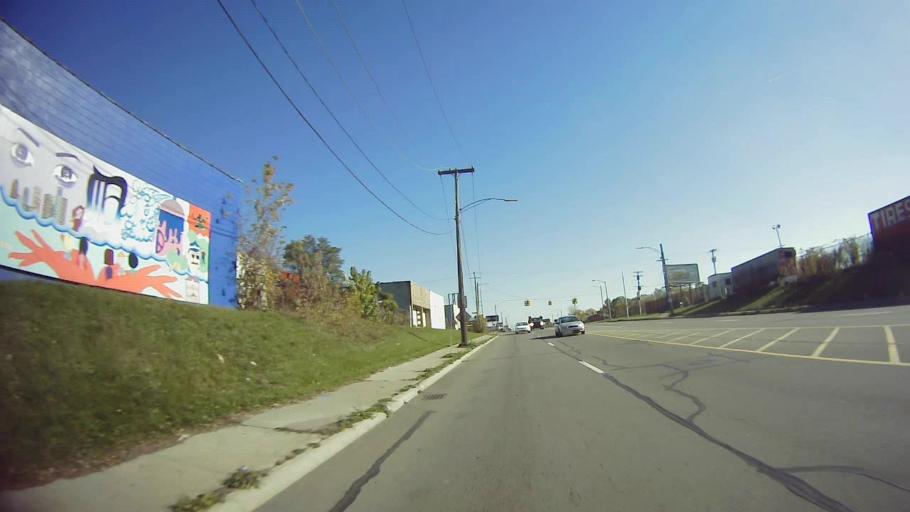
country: US
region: Michigan
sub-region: Wayne County
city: Dearborn Heights
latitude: 42.3722
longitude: -83.2252
